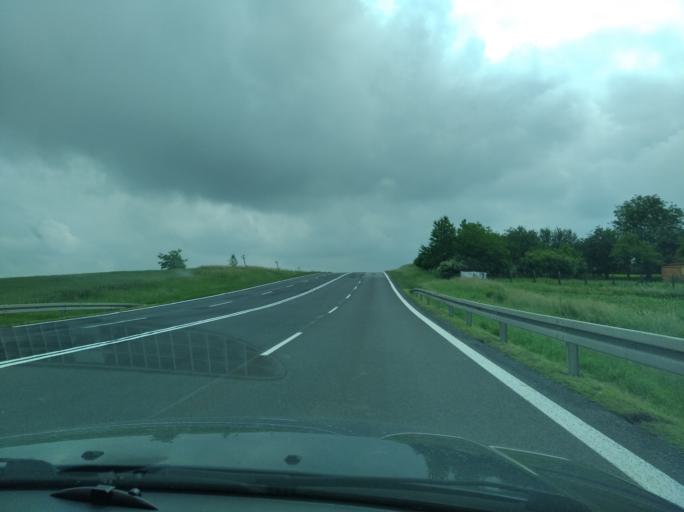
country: PL
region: Subcarpathian Voivodeship
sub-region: Powiat przeworski
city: Rozborz
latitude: 50.0474
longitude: 22.5372
